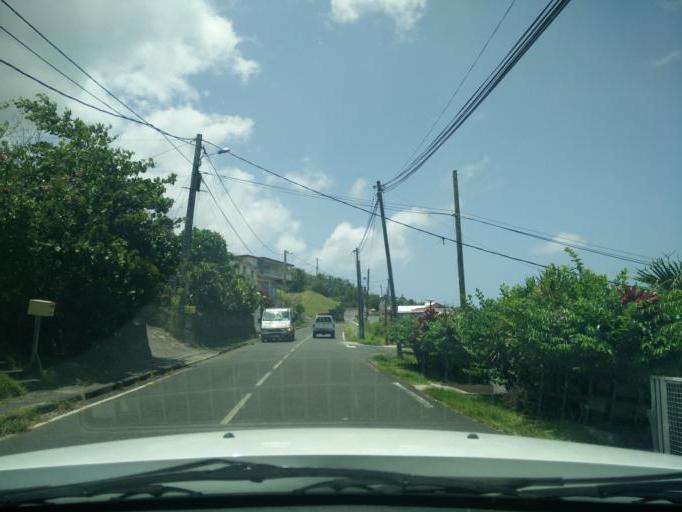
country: GP
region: Guadeloupe
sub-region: Guadeloupe
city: Gourbeyre
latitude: 15.9497
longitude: -61.6924
